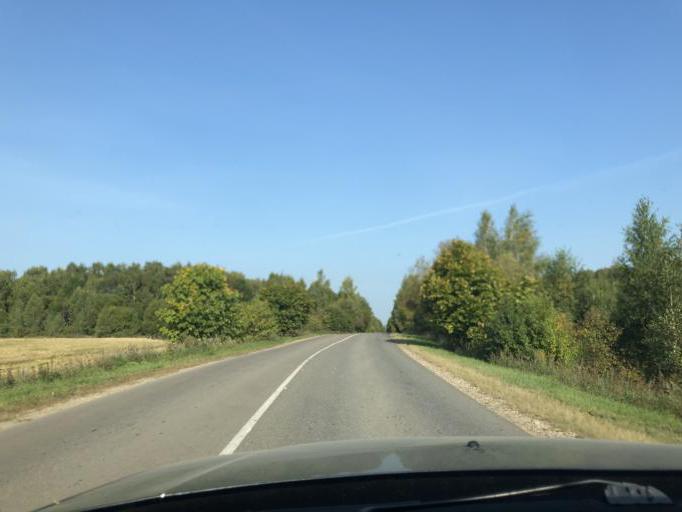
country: RU
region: Tula
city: Novogurovskiy
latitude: 54.3651
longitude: 37.3359
